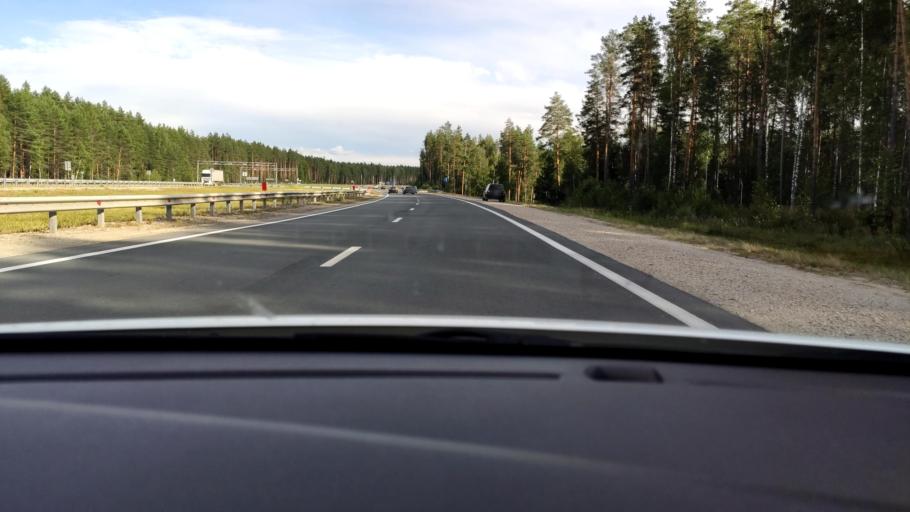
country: RU
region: Mariy-El
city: Yoshkar-Ola
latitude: 56.5354
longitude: 47.9926
